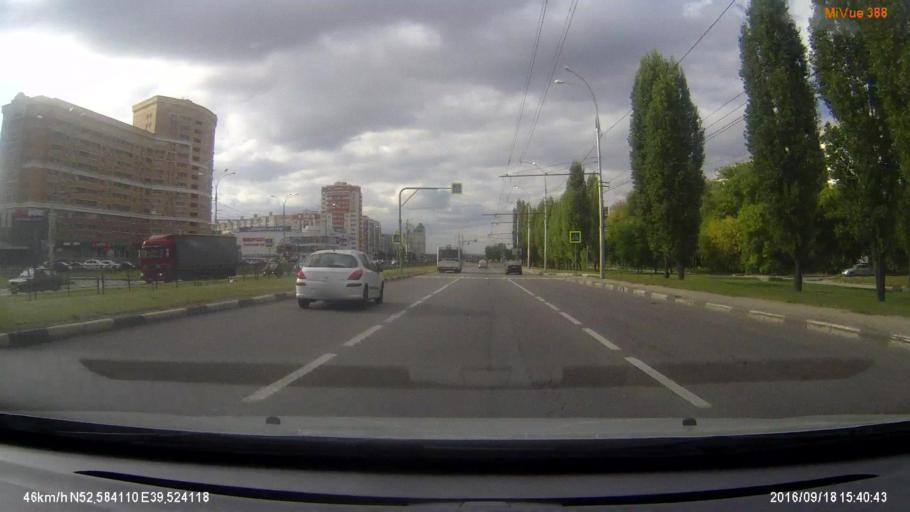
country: RU
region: Lipetsk
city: Syrskoye
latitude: 52.5844
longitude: 39.5237
